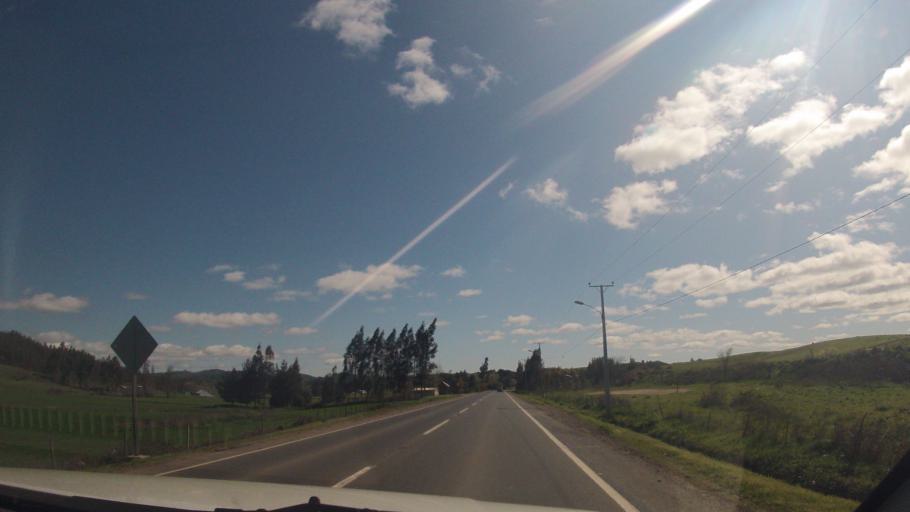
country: CL
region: Araucania
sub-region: Provincia de Malleco
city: Traiguen
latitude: -38.2635
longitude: -72.6706
